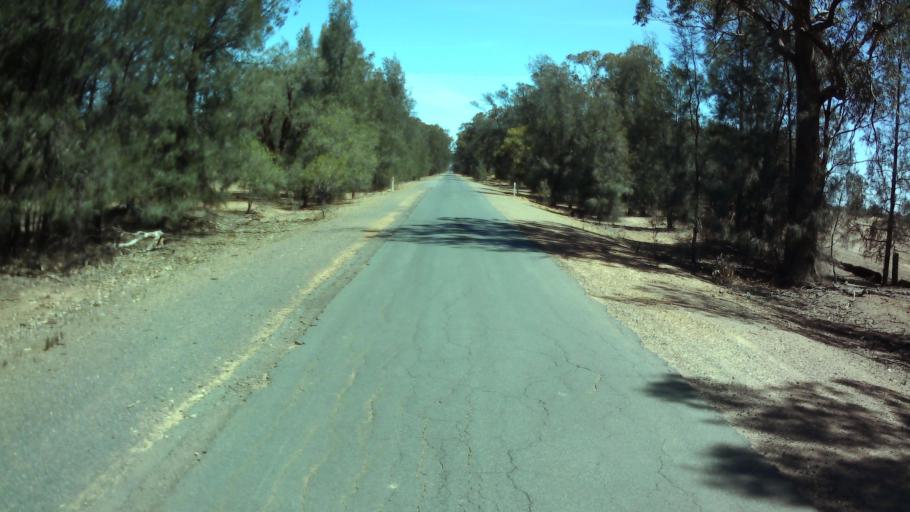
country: AU
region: New South Wales
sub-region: Weddin
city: Grenfell
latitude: -33.8781
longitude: 147.6906
